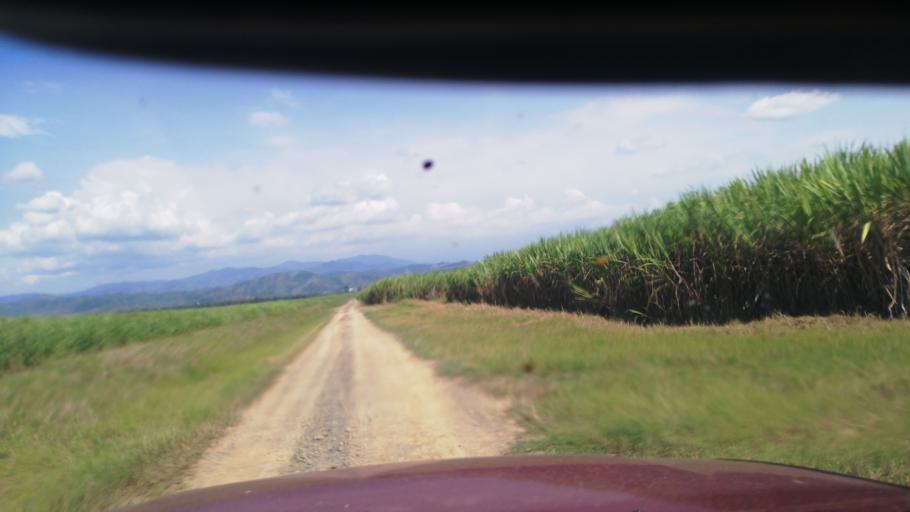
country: CO
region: Risaralda
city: La Virginia
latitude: 4.8927
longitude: -75.9267
